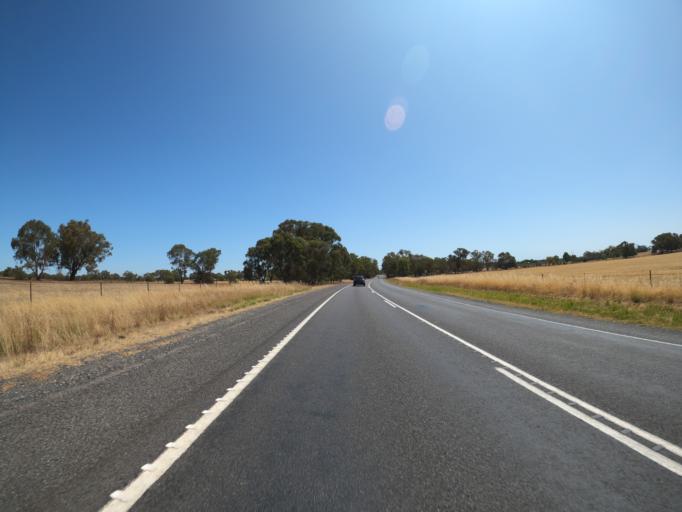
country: AU
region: New South Wales
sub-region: Corowa Shire
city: Corowa
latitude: -36.0571
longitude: 146.4392
